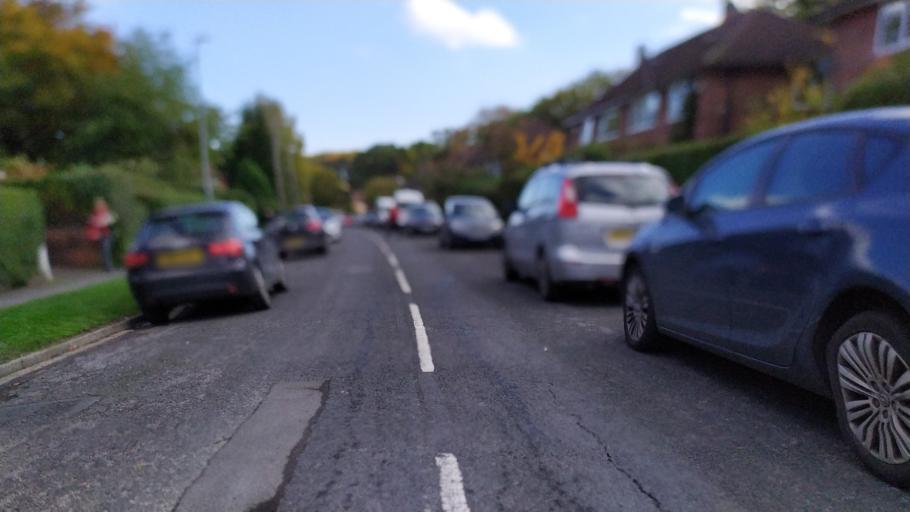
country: GB
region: England
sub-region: City and Borough of Leeds
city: Horsforth
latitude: 53.8227
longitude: -1.5972
